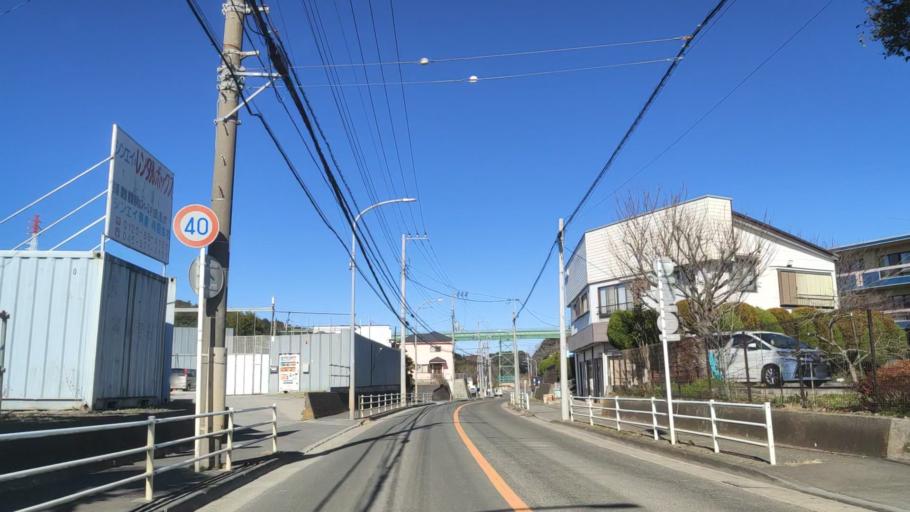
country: JP
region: Kanagawa
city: Minami-rinkan
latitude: 35.4970
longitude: 139.5154
